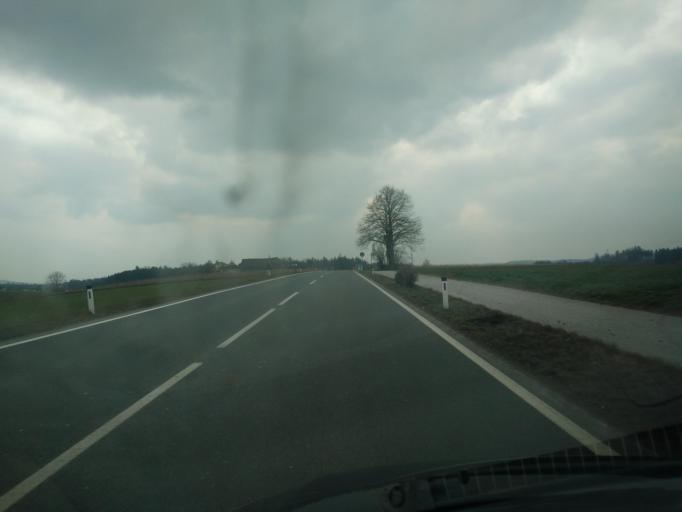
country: AT
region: Salzburg
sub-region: Politischer Bezirk Salzburg-Umgebung
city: Lamprechtshausen
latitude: 47.9650
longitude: 12.9482
